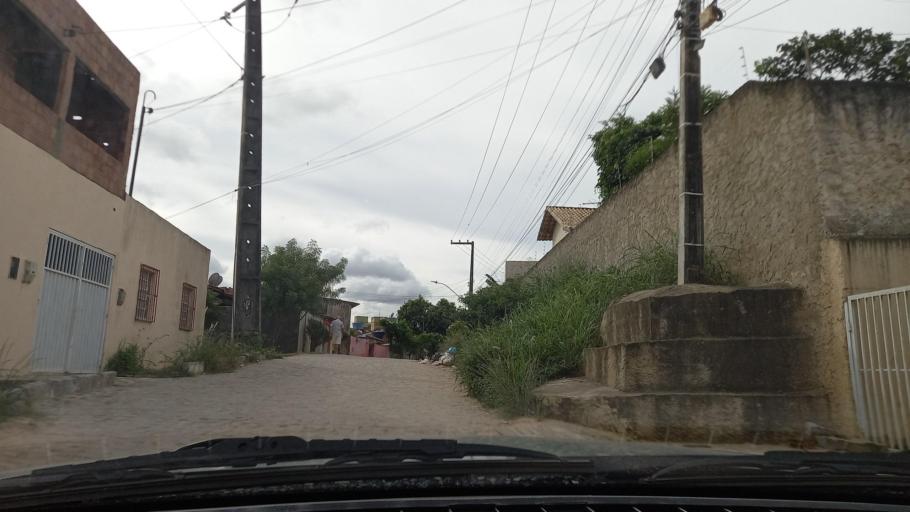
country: BR
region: Pernambuco
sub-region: Gravata
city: Gravata
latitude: -8.2158
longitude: -35.5728
